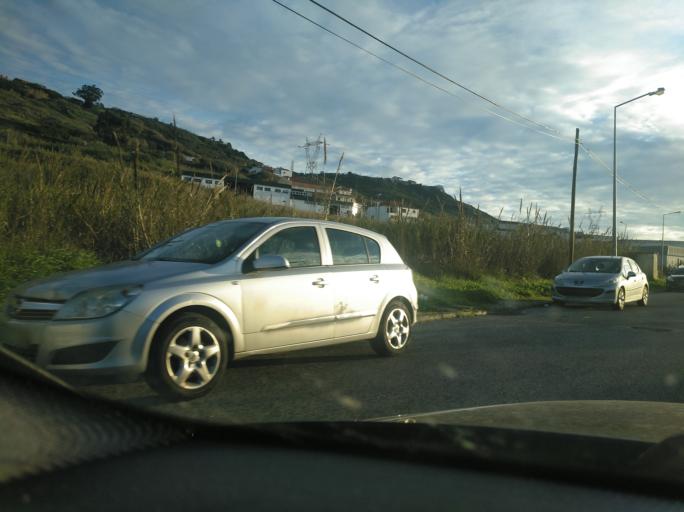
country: PT
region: Lisbon
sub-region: Loures
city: Apelacao
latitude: 38.8173
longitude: -9.1450
